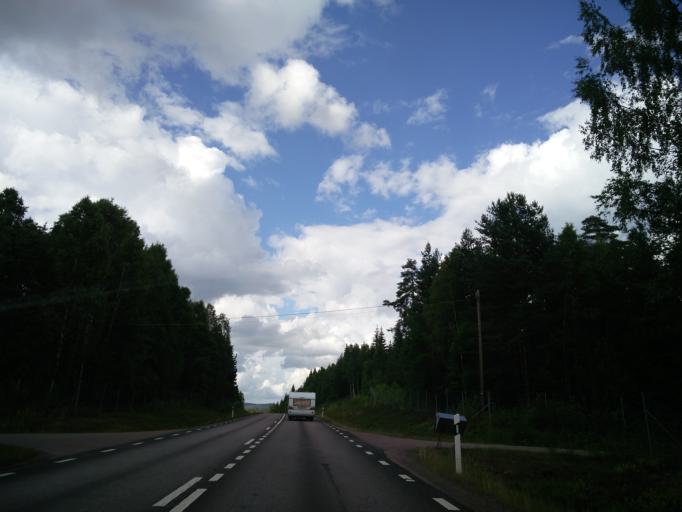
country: SE
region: Vaermland
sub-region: Torsby Kommun
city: Torsby
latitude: 60.1794
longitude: 13.0111
